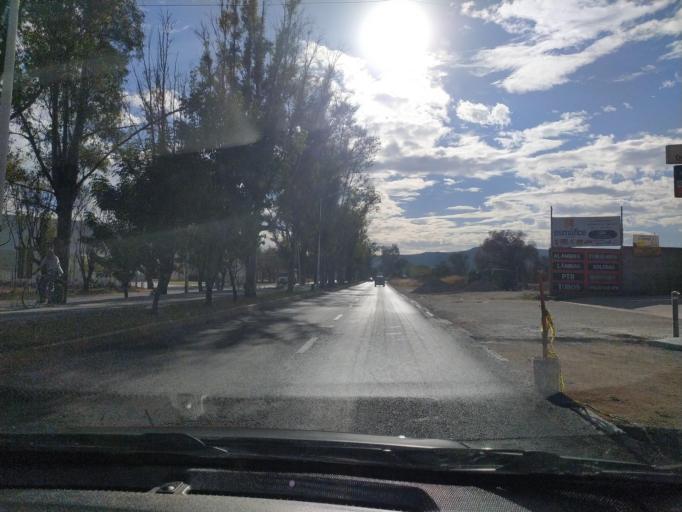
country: LA
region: Oudomxai
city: Muang La
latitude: 21.0303
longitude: 101.8444
